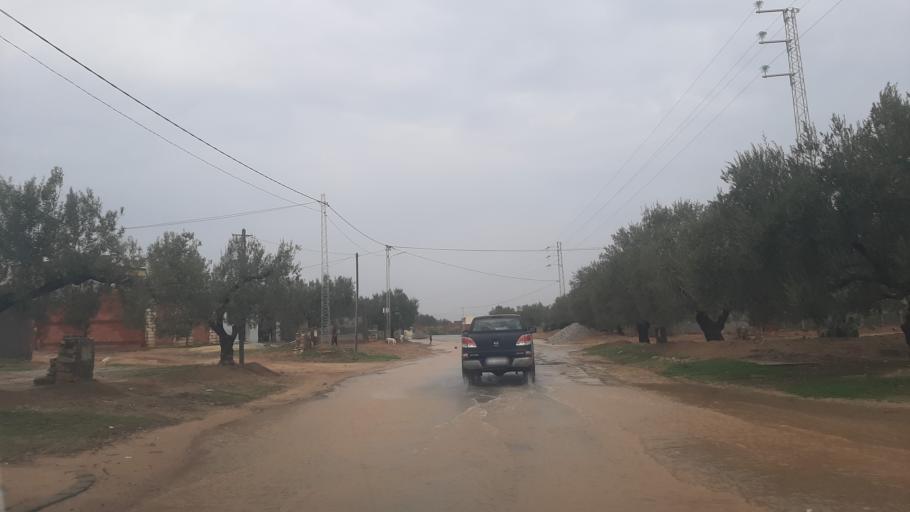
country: TN
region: Al Munastir
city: Sidi Bin Nur
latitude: 35.4717
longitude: 10.8858
